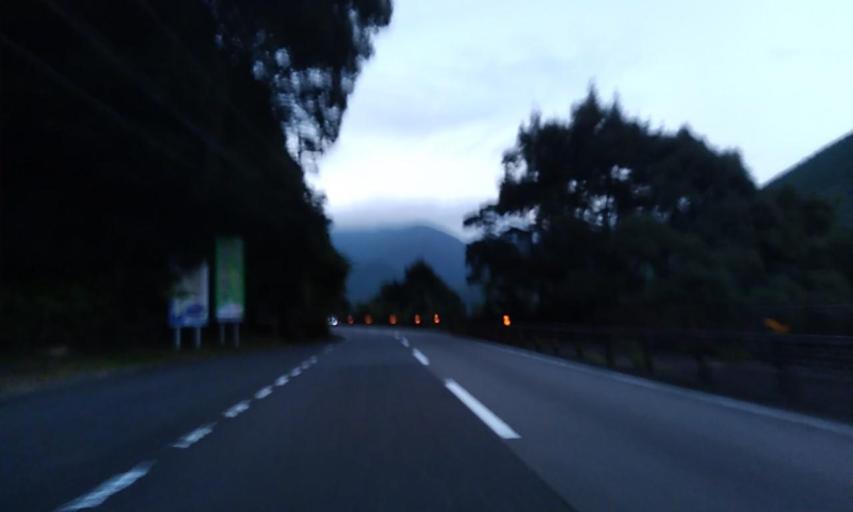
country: JP
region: Wakayama
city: Shingu
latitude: 33.7398
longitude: 135.9388
